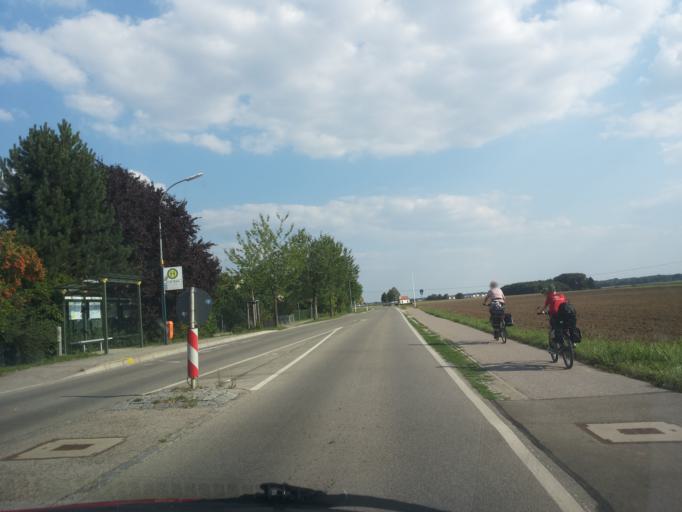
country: DE
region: Bavaria
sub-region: Upper Bavaria
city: Buxheim
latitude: 48.7762
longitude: 11.3304
